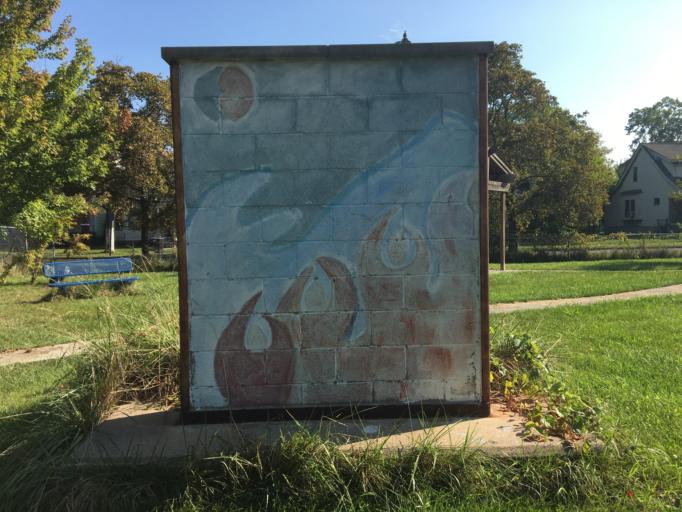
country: US
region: Michigan
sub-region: Wayne County
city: Hamtramck
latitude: 42.3720
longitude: -82.9983
